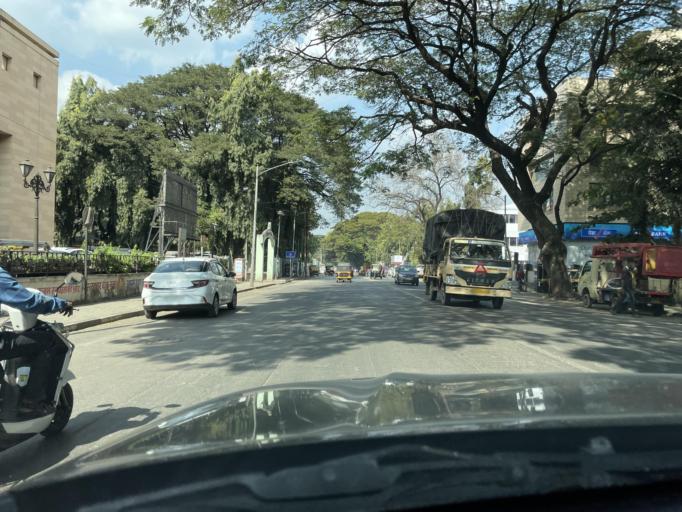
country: IN
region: Maharashtra
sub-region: Pune Division
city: Pune
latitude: 18.4973
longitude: 73.9002
